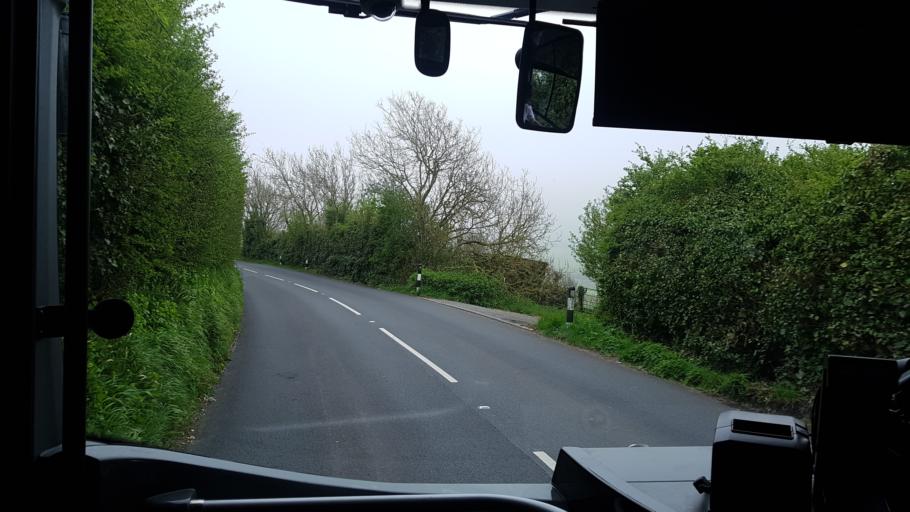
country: GB
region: England
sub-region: Isle of Wight
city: Ventnor
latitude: 50.6030
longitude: -1.2233
